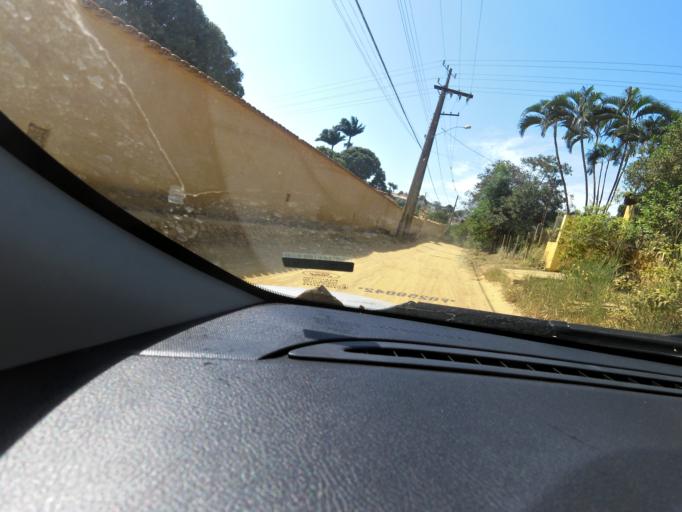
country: BR
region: Espirito Santo
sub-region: Guarapari
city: Guarapari
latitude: -20.6492
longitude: -40.5188
